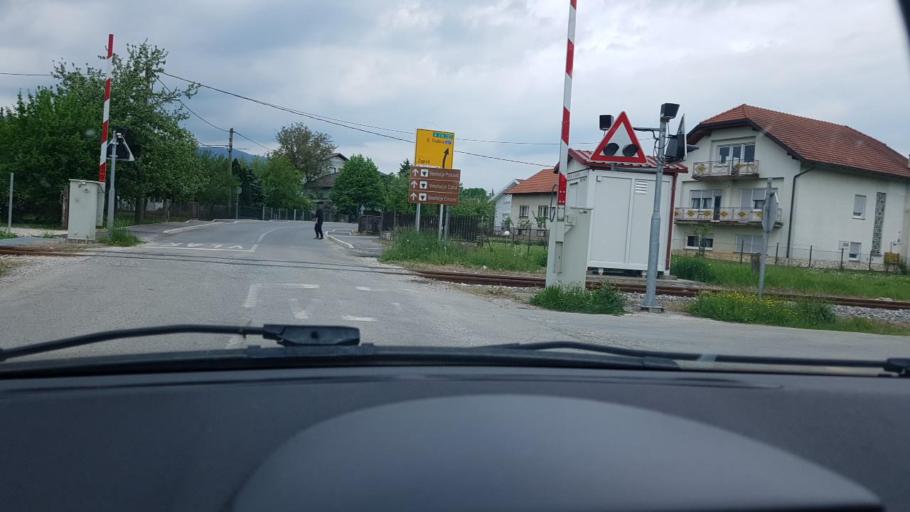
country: HR
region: Krapinsko-Zagorska
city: Selnica
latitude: 45.9844
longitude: 16.0015
